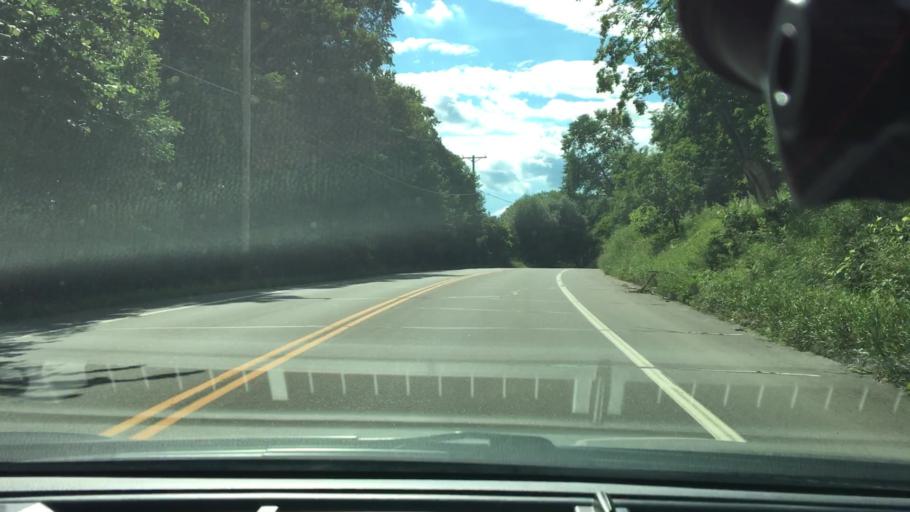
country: US
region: Minnesota
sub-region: Hennepin County
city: Minnetrista
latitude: 44.9223
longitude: -93.6970
